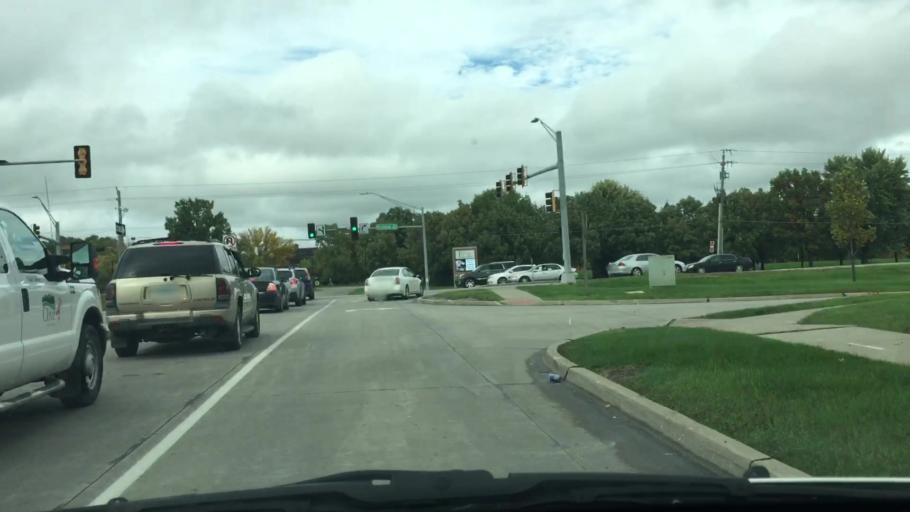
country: US
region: Iowa
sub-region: Polk County
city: Clive
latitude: 41.6144
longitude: -93.7715
